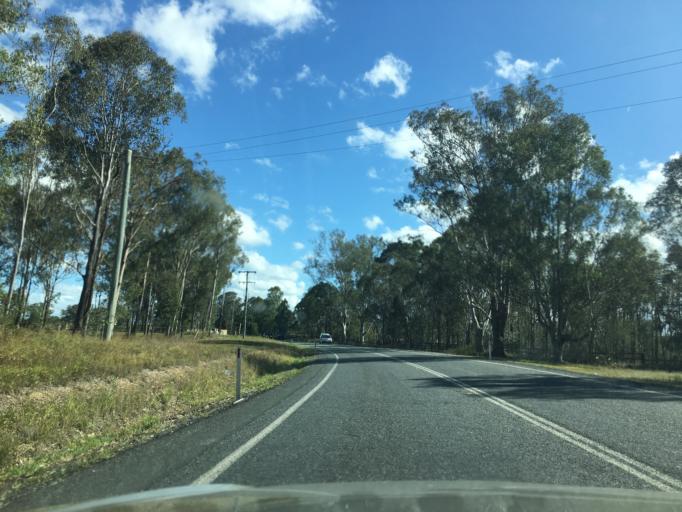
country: AU
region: Queensland
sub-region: Logan
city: Chambers Flat
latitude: -27.7584
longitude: 153.1111
